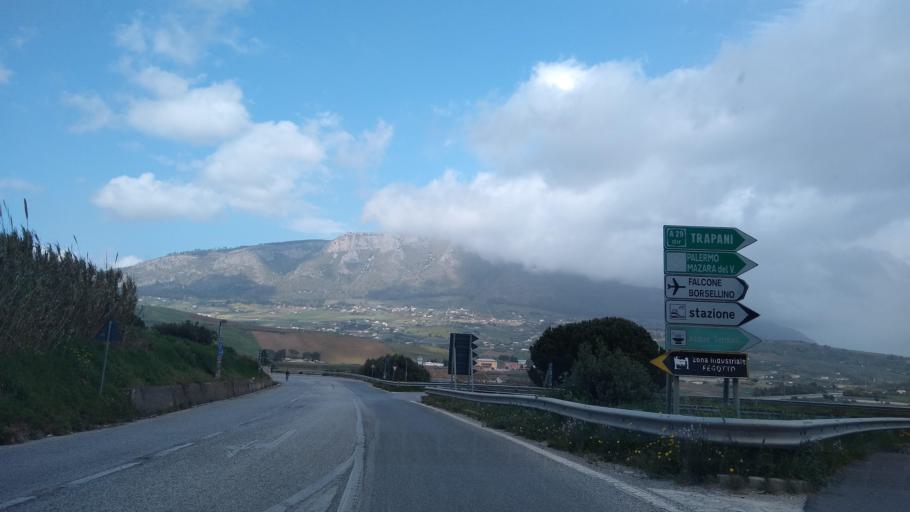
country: IT
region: Sicily
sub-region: Trapani
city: Alcamo
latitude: 37.9725
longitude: 12.9273
